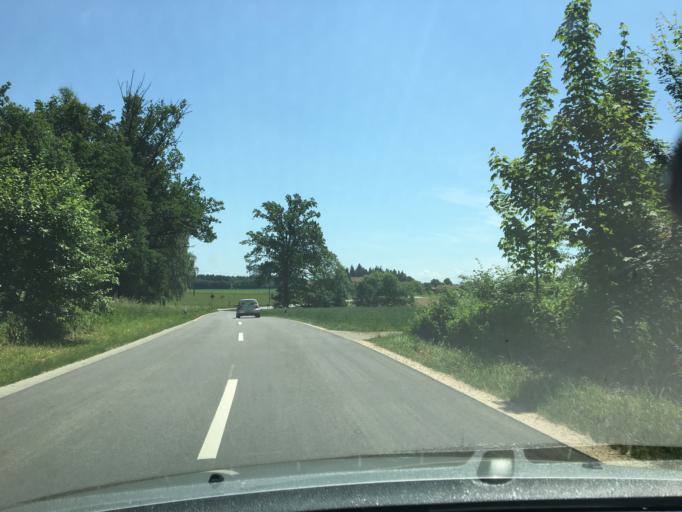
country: DE
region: Bavaria
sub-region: Upper Bavaria
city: Halsbach
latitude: 48.1127
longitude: 12.6815
